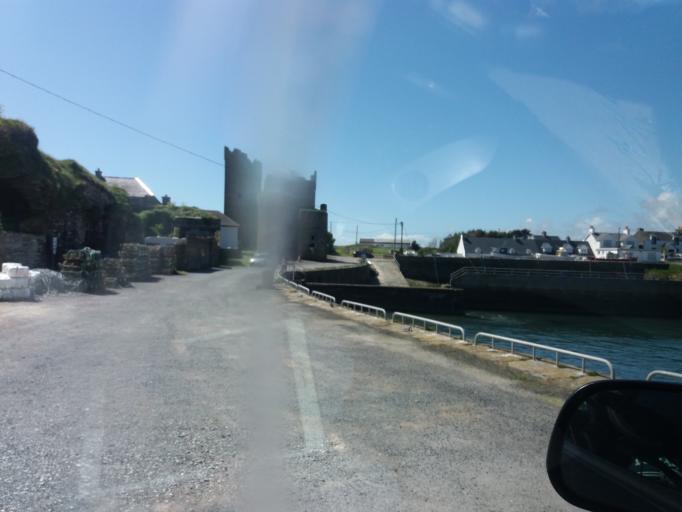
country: IE
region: Munster
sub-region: Waterford
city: Dunmore East
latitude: 52.1340
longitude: -6.9093
